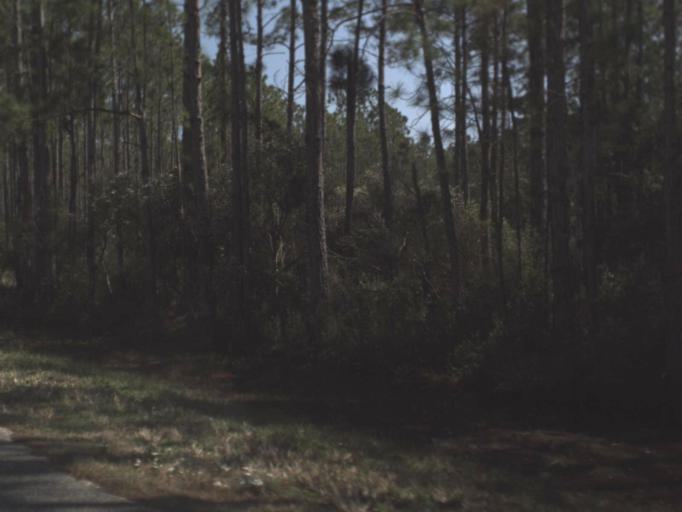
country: US
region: Florida
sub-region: Gulf County
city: Port Saint Joe
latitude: 29.7387
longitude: -85.1827
